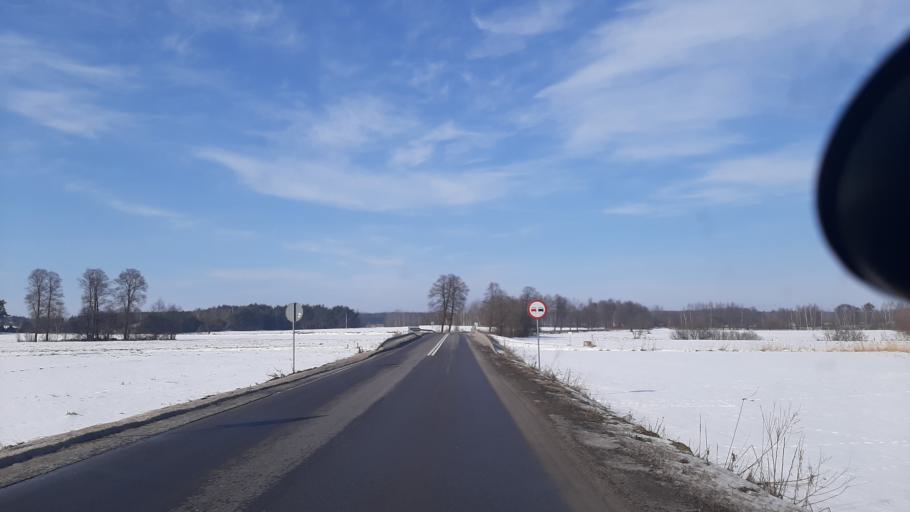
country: PL
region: Lublin Voivodeship
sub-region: Powiat pulawski
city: Kurow
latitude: 51.4116
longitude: 22.2051
